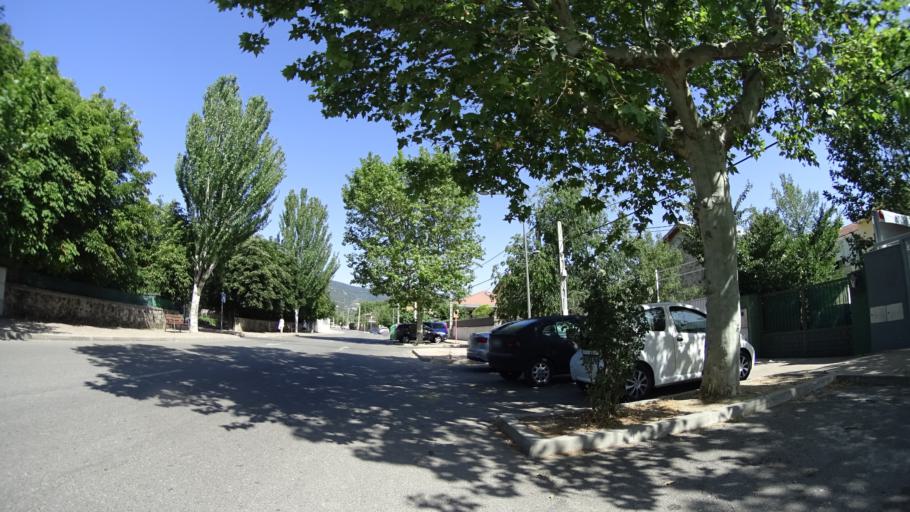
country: ES
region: Madrid
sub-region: Provincia de Madrid
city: Guadarrama
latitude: 40.6773
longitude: -4.0919
